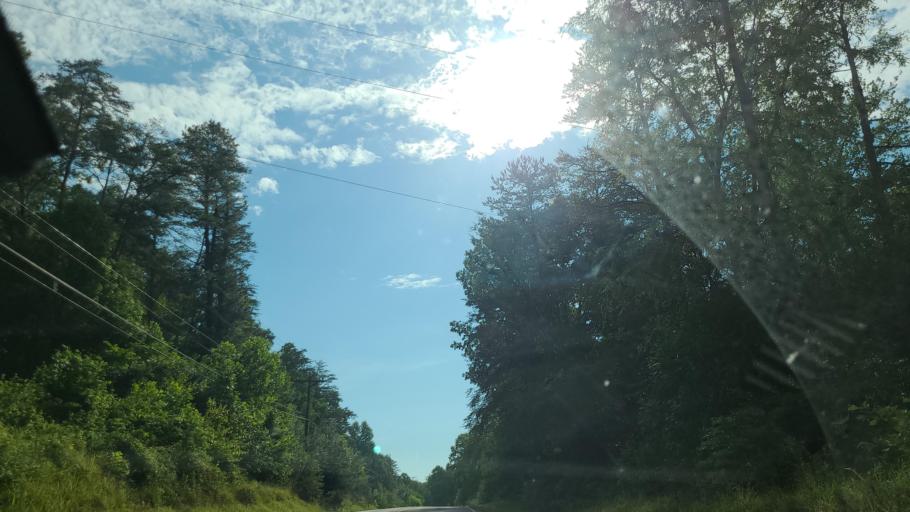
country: US
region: Kentucky
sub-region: Whitley County
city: Williamsburg
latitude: 36.7473
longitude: -84.0386
